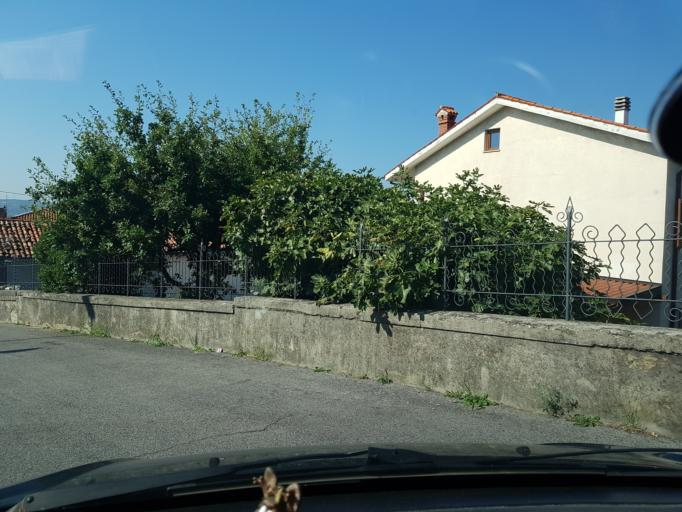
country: IT
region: Friuli Venezia Giulia
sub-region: Provincia di Trieste
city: Trieste
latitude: 45.6307
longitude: 13.8037
